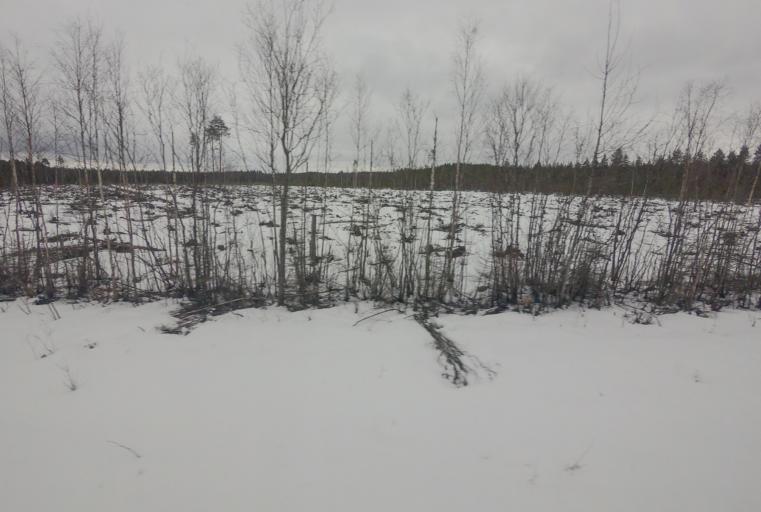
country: FI
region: Southern Savonia
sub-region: Savonlinna
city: Savonlinna
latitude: 61.8620
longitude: 29.0079
